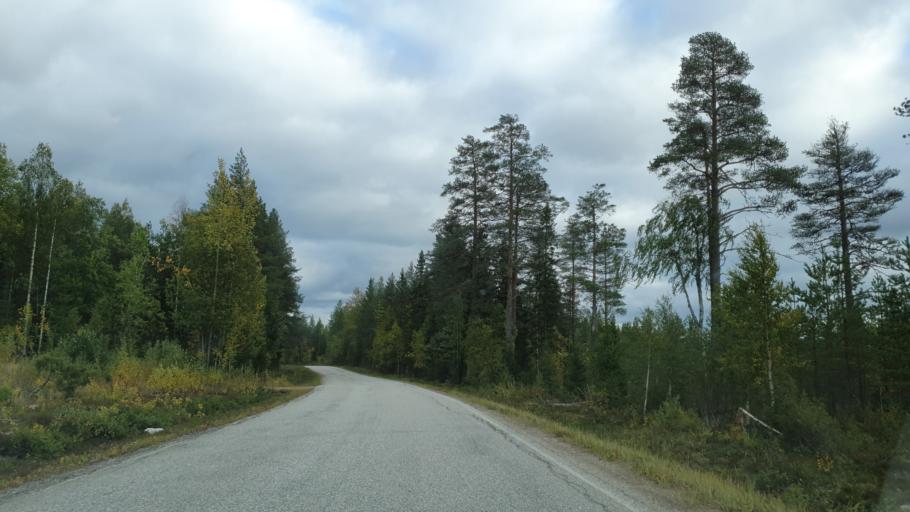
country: FI
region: Kainuu
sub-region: Kehys-Kainuu
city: Kuhmo
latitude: 63.9481
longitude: 29.7610
